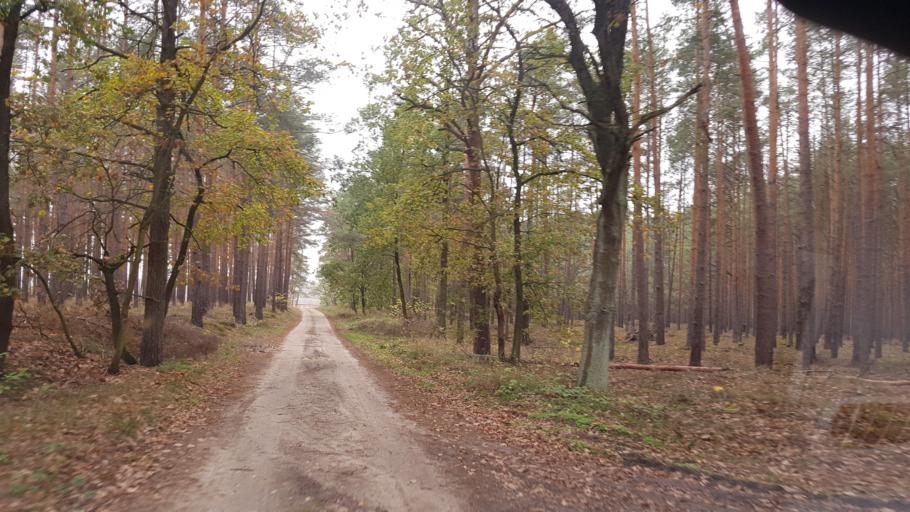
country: DE
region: Brandenburg
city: Schonborn
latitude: 51.6818
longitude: 13.4886
